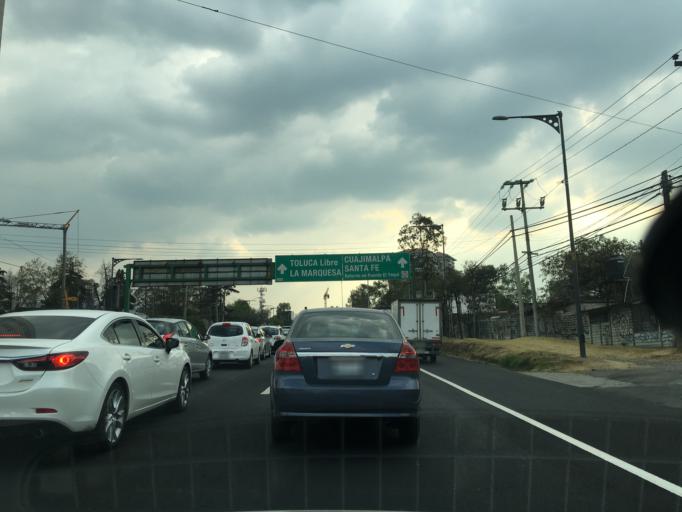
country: MX
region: Mexico City
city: Col. Bosques de las Lomas
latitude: 19.3674
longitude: -99.2715
